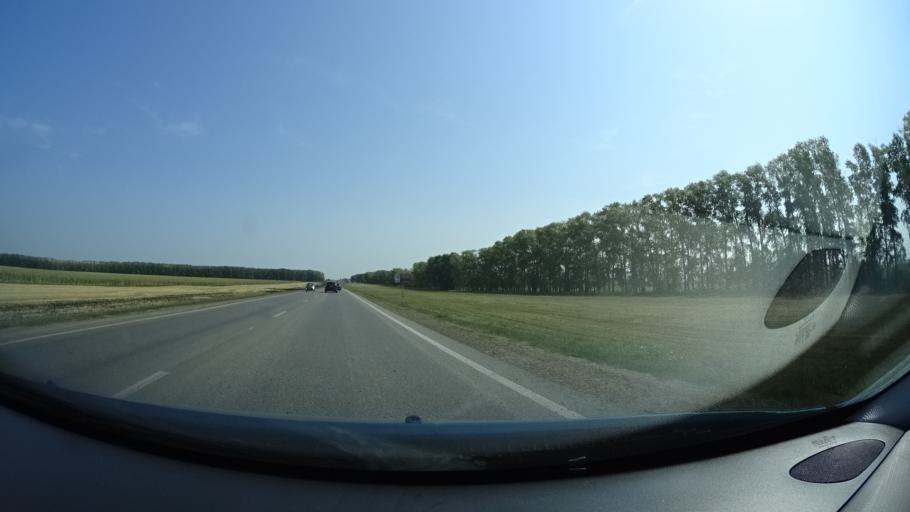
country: RU
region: Bashkortostan
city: Karmaskaly
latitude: 54.3851
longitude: 56.1627
